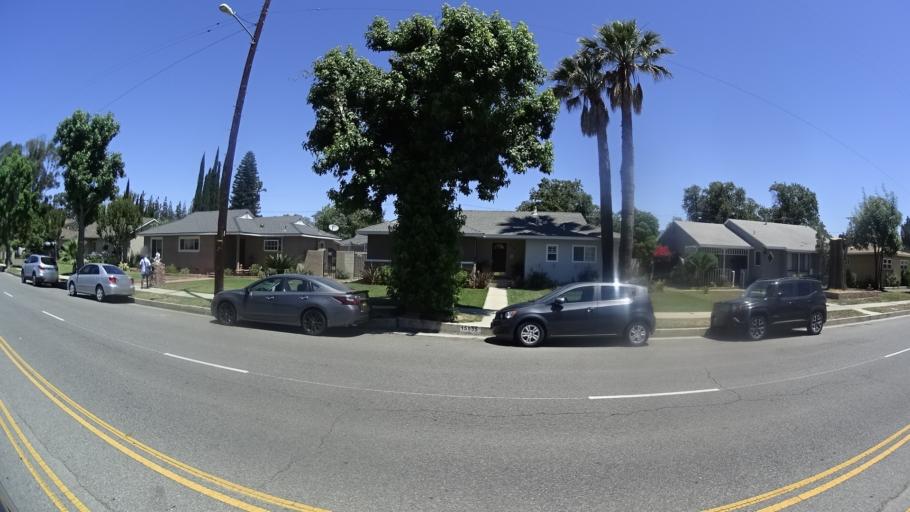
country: US
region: California
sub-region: Los Angeles County
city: San Fernando
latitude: 34.2501
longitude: -118.4710
